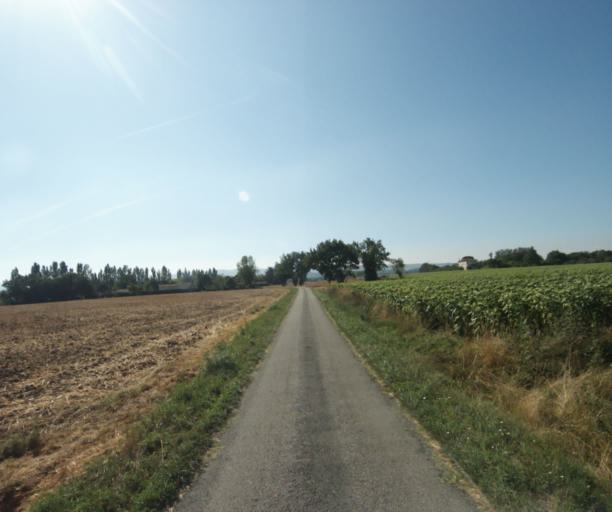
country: FR
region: Midi-Pyrenees
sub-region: Departement de la Haute-Garonne
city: Revel
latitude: 43.4691
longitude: 1.9567
